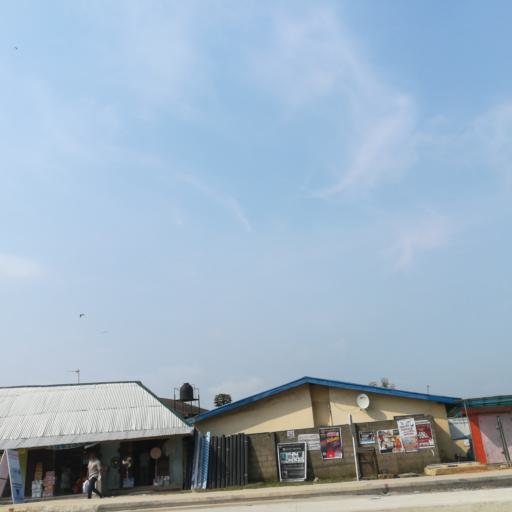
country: NG
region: Rivers
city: Port Harcourt
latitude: 4.8446
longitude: 7.0651
